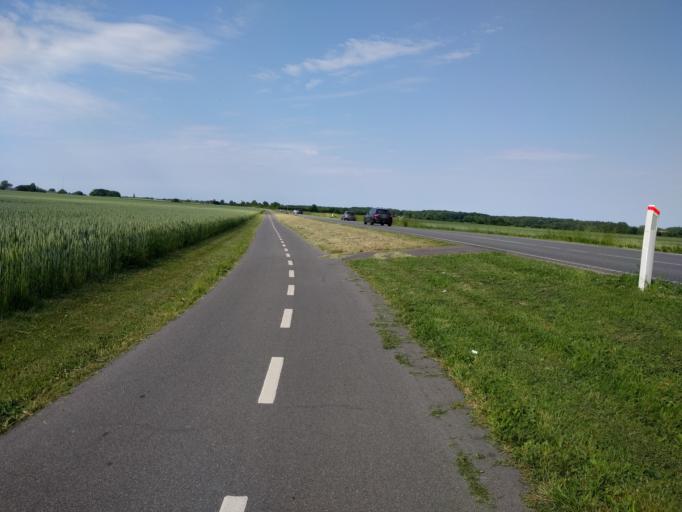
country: DK
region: South Denmark
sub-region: Kerteminde Kommune
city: Kerteminde
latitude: 55.4245
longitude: 10.6497
